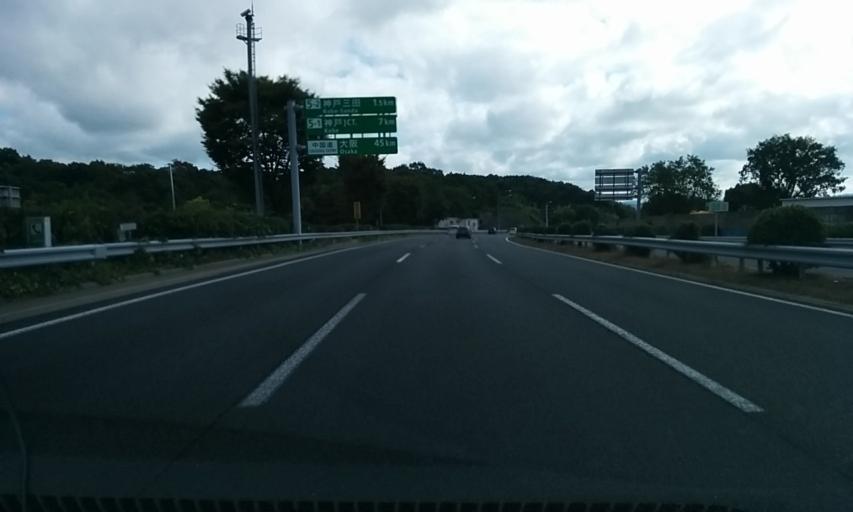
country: JP
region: Hyogo
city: Sandacho
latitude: 34.8852
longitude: 135.1692
